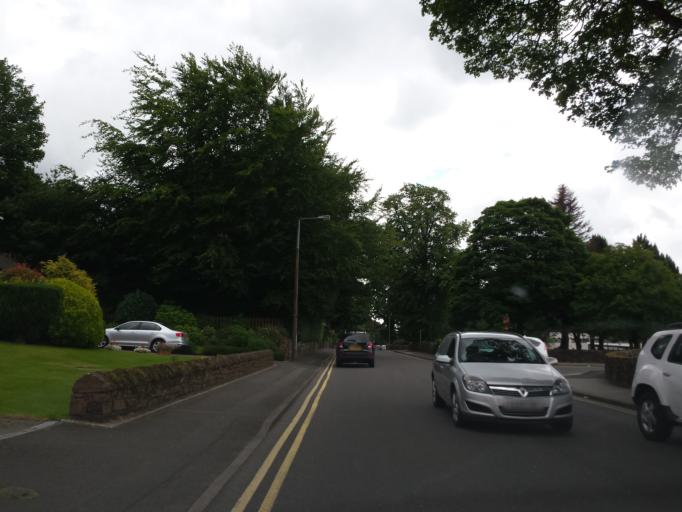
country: GB
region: Scotland
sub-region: Dumfries and Galloway
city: Dumfries
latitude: 55.0586
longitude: -3.5986
